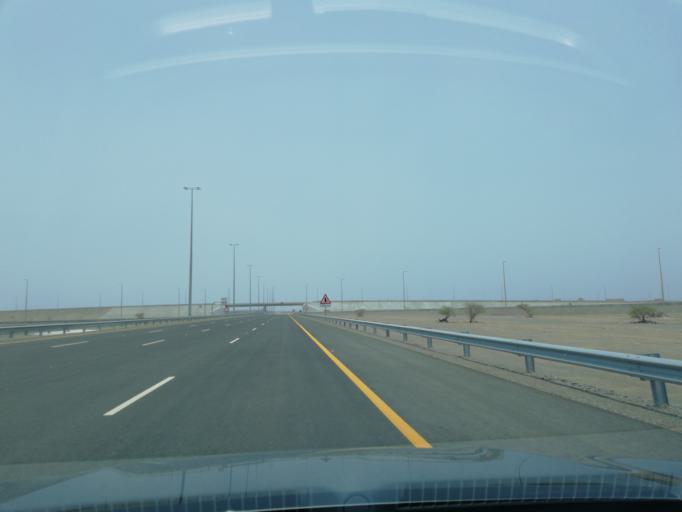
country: OM
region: Al Batinah
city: Al Liwa'
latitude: 24.5262
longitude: 56.5027
